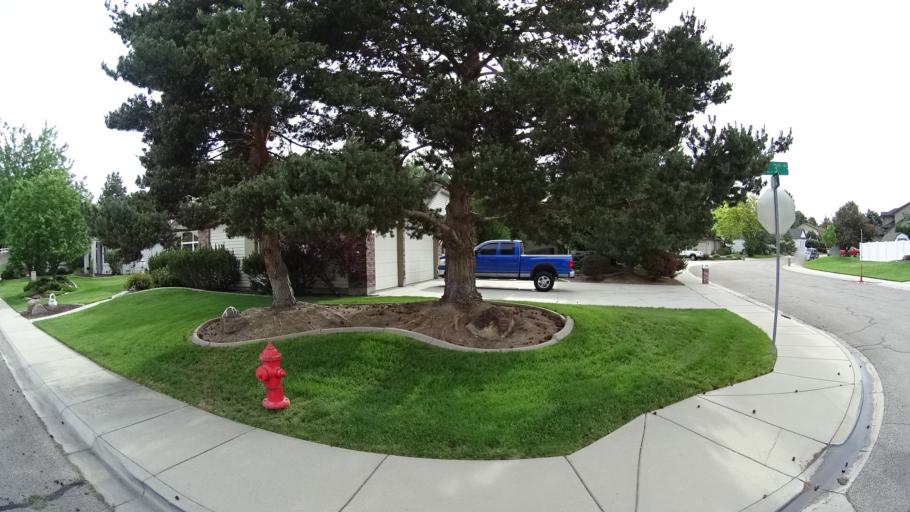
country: US
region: Idaho
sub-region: Ada County
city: Meridian
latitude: 43.5861
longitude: -116.3889
